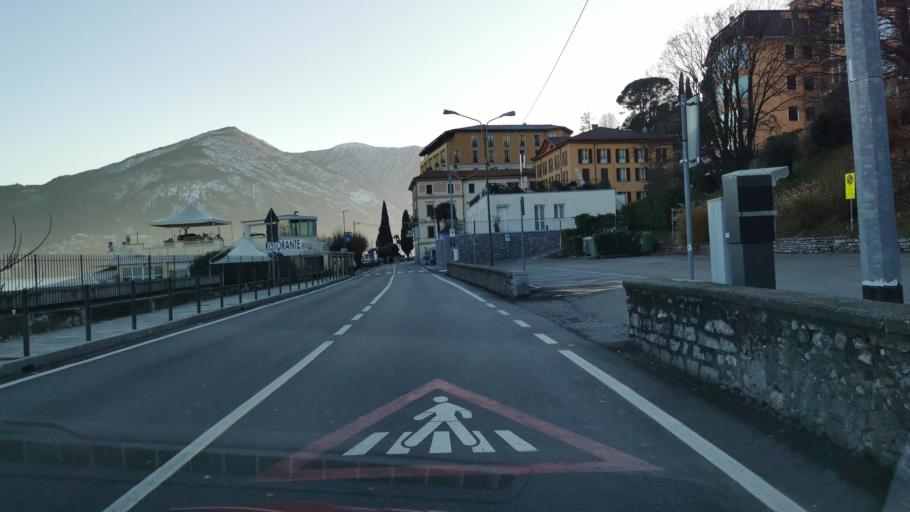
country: IT
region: Lombardy
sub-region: Provincia di Como
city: Griante
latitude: 45.9937
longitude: 9.2388
